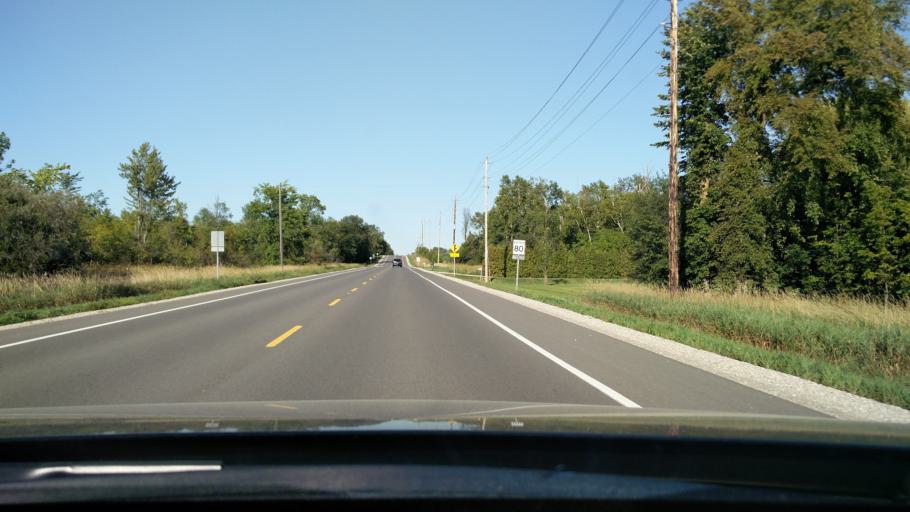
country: CA
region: Ontario
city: Perth
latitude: 44.9125
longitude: -76.2347
